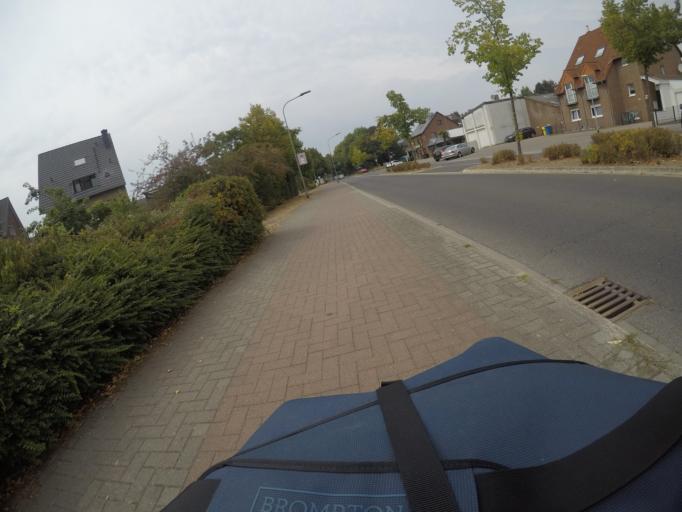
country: DE
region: North Rhine-Westphalia
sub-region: Regierungsbezirk Dusseldorf
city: Neuss
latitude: 51.1783
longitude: 6.7387
